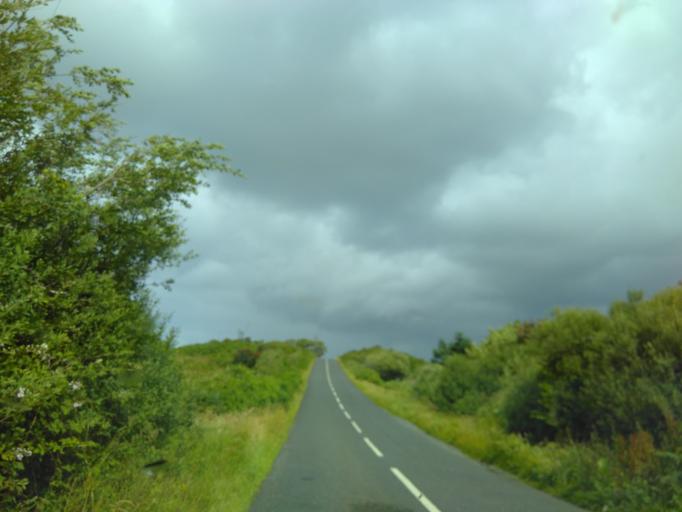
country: IE
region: Ulster
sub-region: County Donegal
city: Buncrana
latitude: 55.1751
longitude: -7.5795
